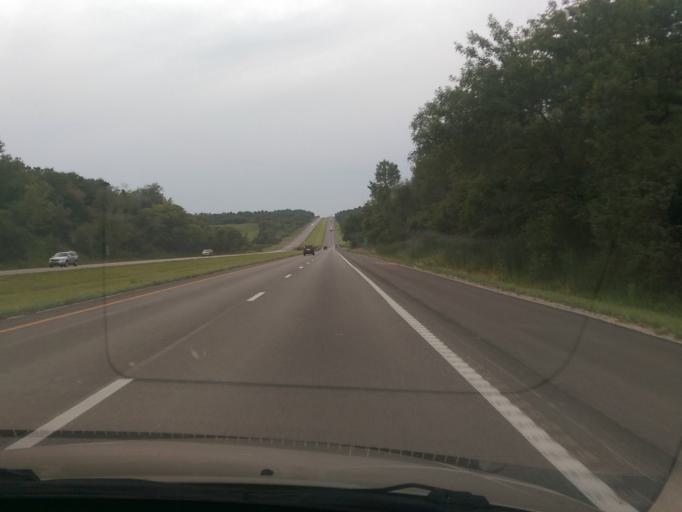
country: US
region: Missouri
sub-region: Andrew County
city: Savannah
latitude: 39.9345
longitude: -94.9286
